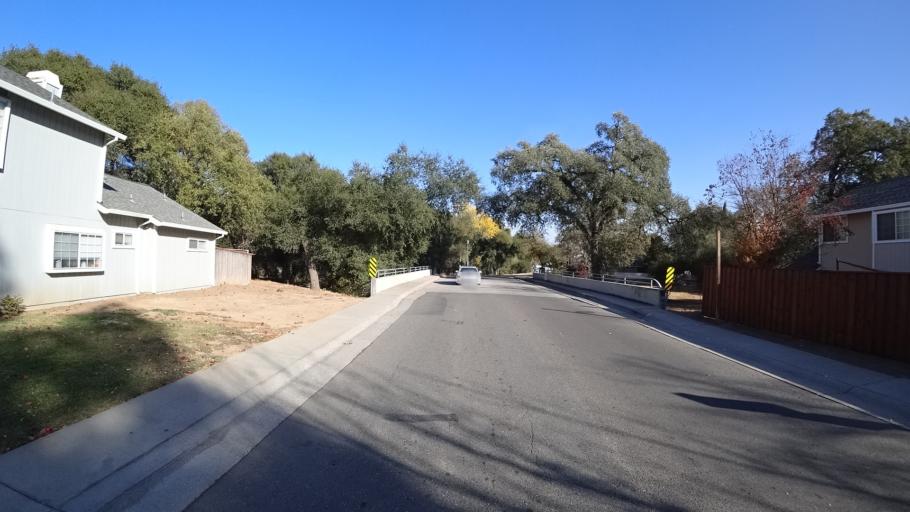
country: US
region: California
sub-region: Sacramento County
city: Antelope
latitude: 38.6953
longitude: -121.3111
